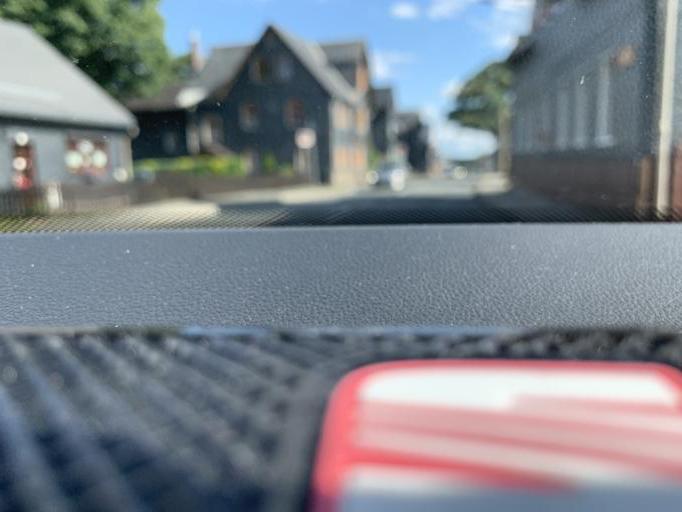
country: DE
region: Thuringia
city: Neuhaus am Rennweg
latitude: 50.5017
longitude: 11.1491
